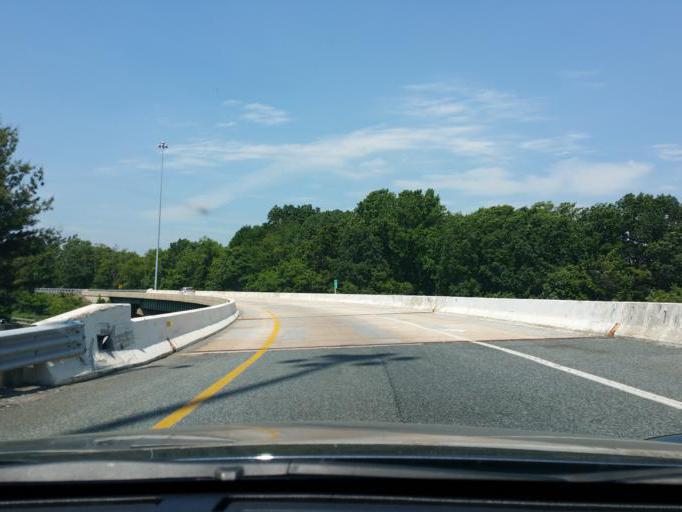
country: US
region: Maryland
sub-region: Howard County
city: Elkridge
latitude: 39.2228
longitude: -76.7194
